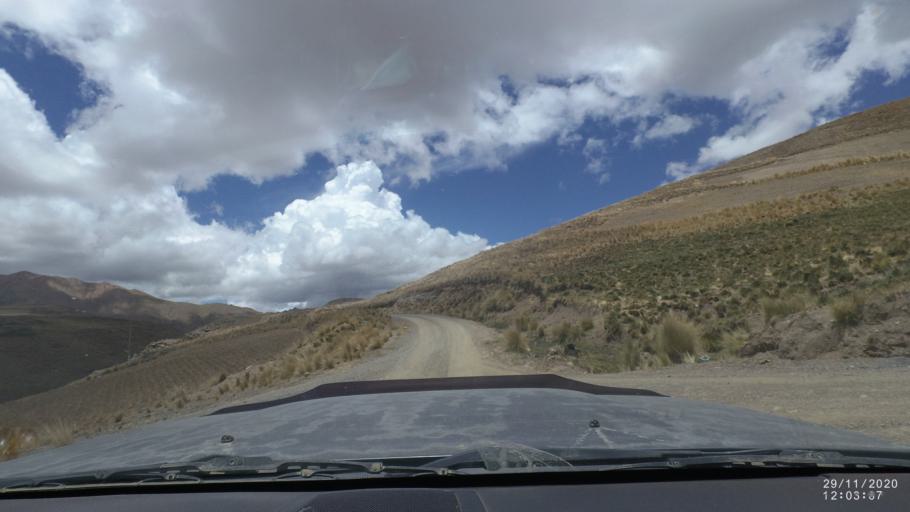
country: BO
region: Cochabamba
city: Cochabamba
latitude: -17.1503
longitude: -66.2842
